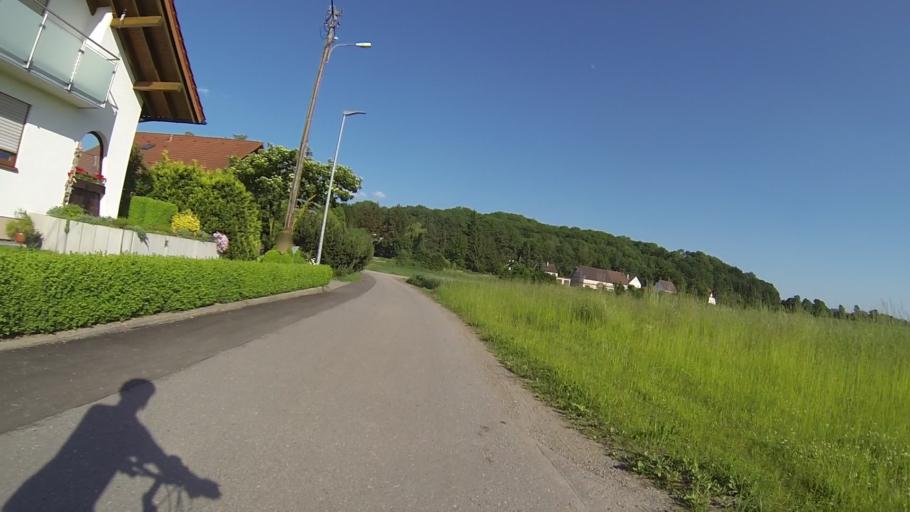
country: DE
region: Baden-Wuerttemberg
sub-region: Tuebingen Region
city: Warthausen
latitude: 48.1396
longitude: 9.8045
